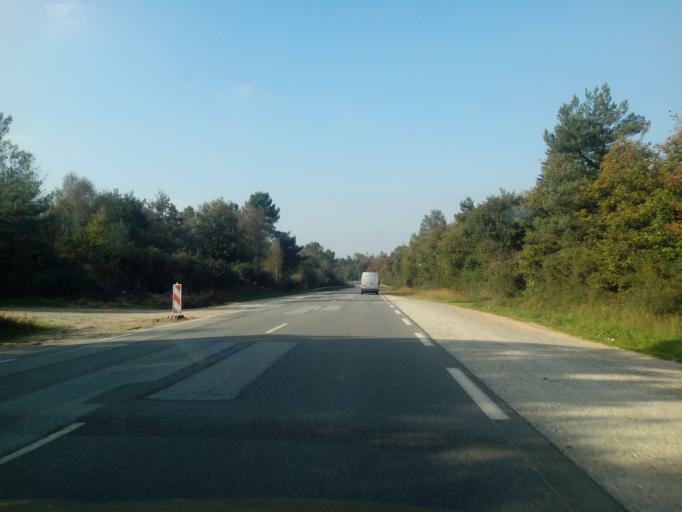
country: FR
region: Brittany
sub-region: Departement du Morbihan
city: Molac
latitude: 47.7596
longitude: -2.4428
